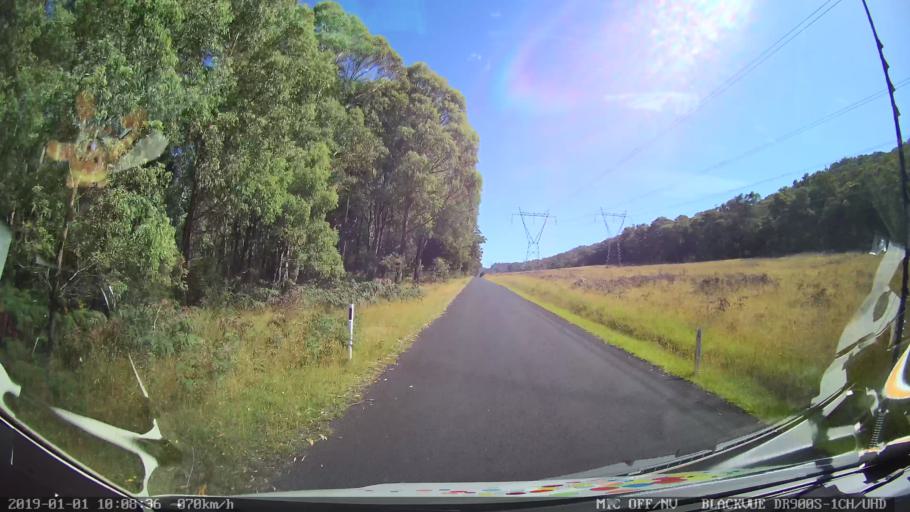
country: AU
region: New South Wales
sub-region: Snowy River
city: Jindabyne
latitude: -36.1578
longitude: 148.1577
